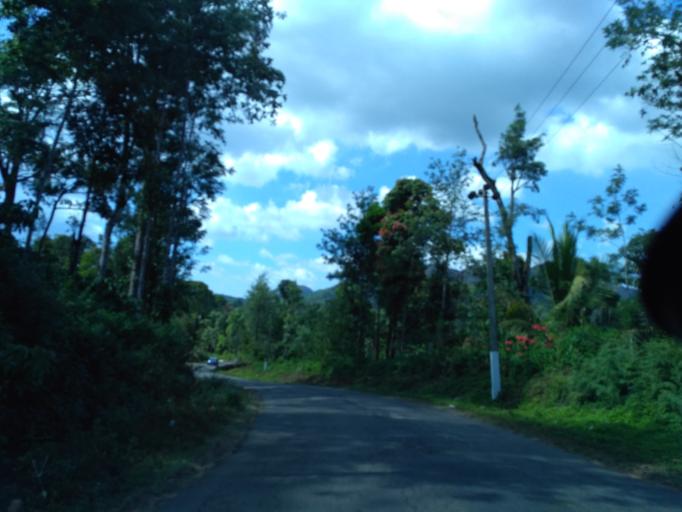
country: IN
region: Karnataka
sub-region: Kodagu
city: Madikeri
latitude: 12.3730
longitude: 75.6179
